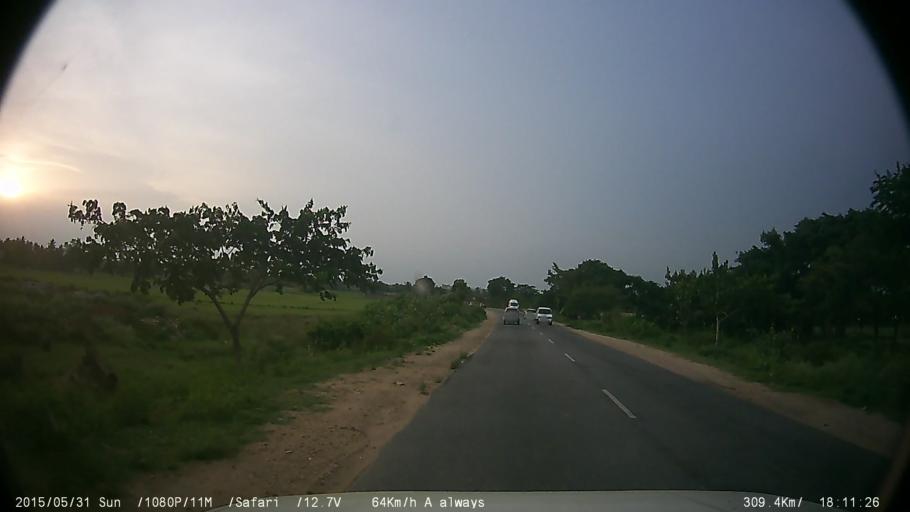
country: IN
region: Karnataka
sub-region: Mysore
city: Nanjangud
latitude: 12.0876
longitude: 76.6744
